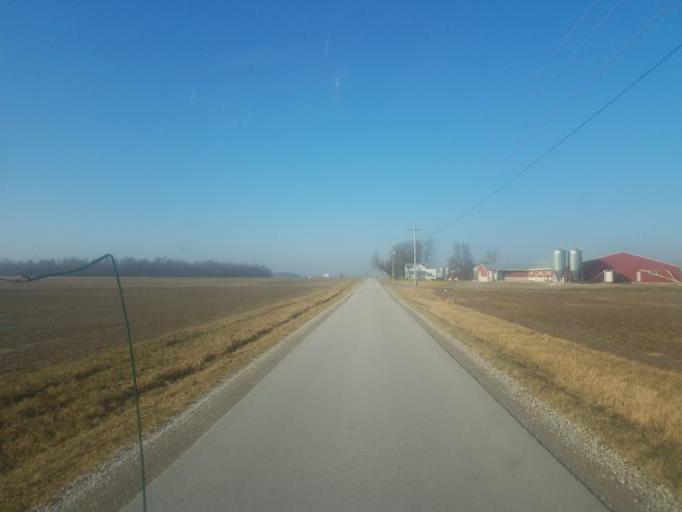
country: US
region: Ohio
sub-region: Huron County
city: Willard
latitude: 41.0084
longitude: -82.9190
